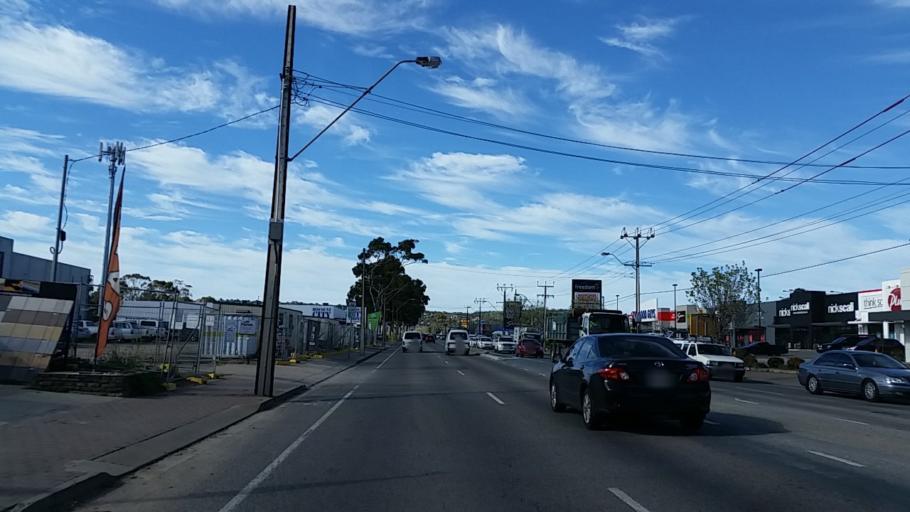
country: AU
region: South Australia
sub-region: Marion
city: Sturt
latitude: -35.0095
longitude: 138.5583
